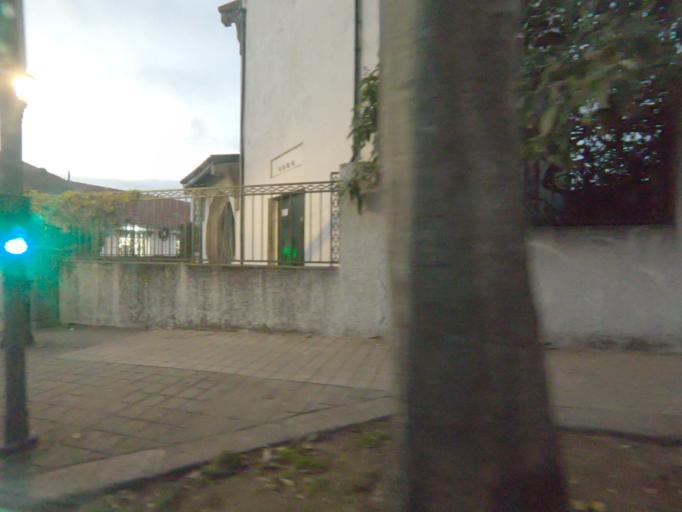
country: PT
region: Porto
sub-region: Matosinhos
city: Matosinhos
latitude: 41.1543
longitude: -8.6743
